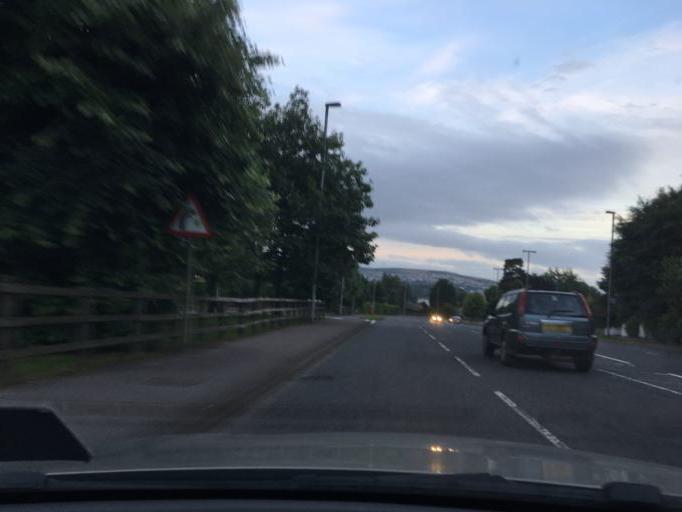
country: GB
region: Northern Ireland
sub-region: City of Derry
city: Derry
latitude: 55.0191
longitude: -7.3089
